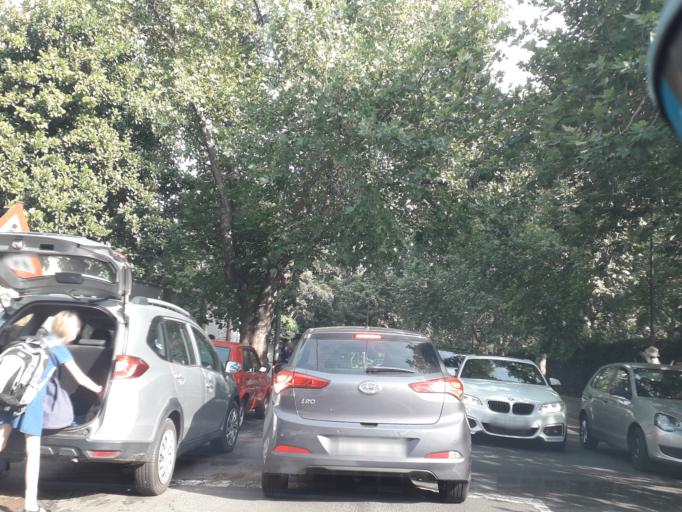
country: ZA
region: Gauteng
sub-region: City of Johannesburg Metropolitan Municipality
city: Johannesburg
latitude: -26.1553
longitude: 28.0241
